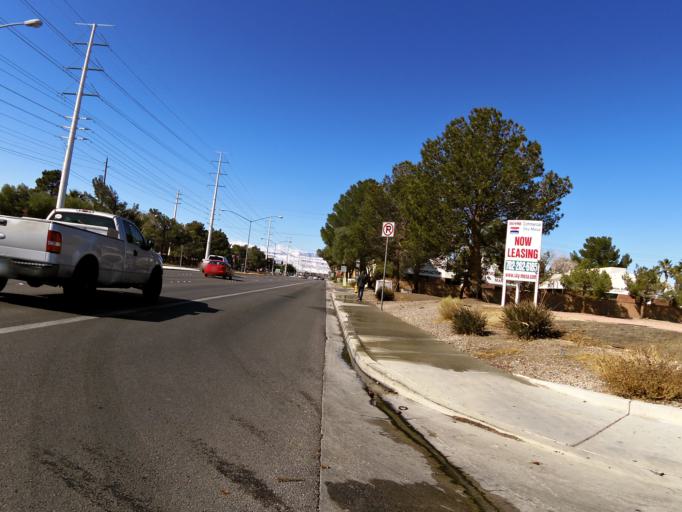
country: US
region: Nevada
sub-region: Clark County
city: Spring Valley
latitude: 36.1151
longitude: -115.2180
